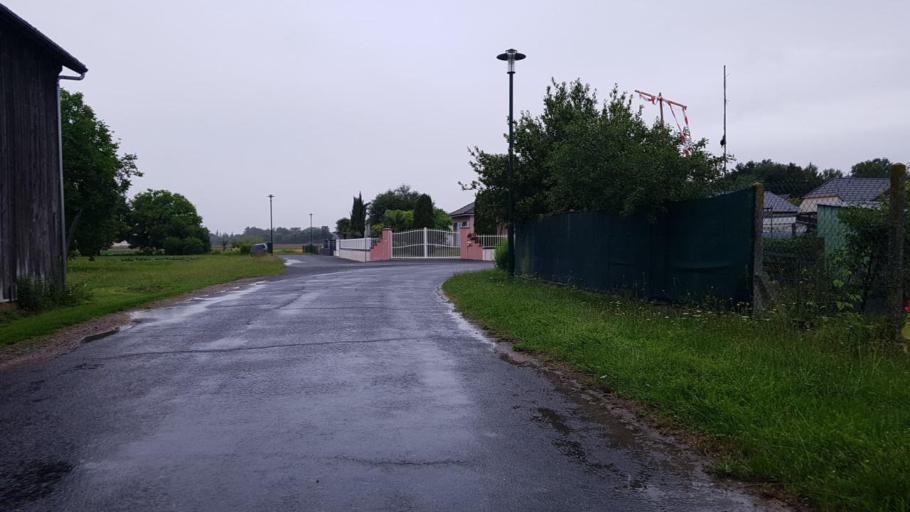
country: FR
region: Champagne-Ardenne
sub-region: Departement de la Marne
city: Sarry
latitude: 48.8727
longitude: 4.4577
